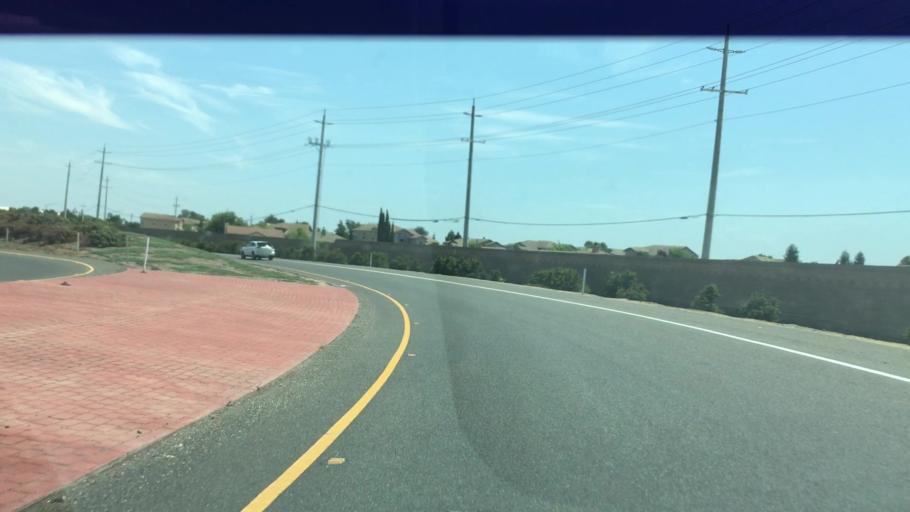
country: US
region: California
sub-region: Sacramento County
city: Laguna
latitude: 38.4363
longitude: -121.4032
